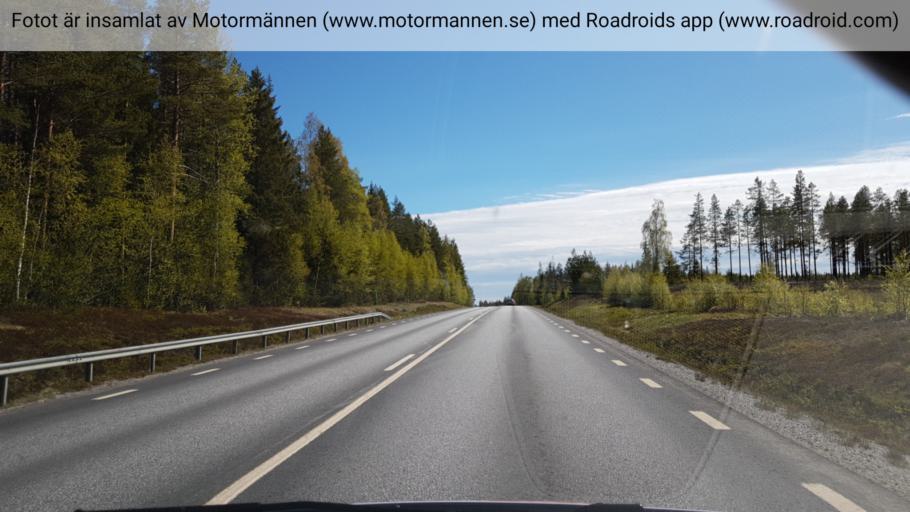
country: SE
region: Vaesterbotten
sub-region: Vannas Kommun
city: Vannasby
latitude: 64.0526
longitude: 19.9972
